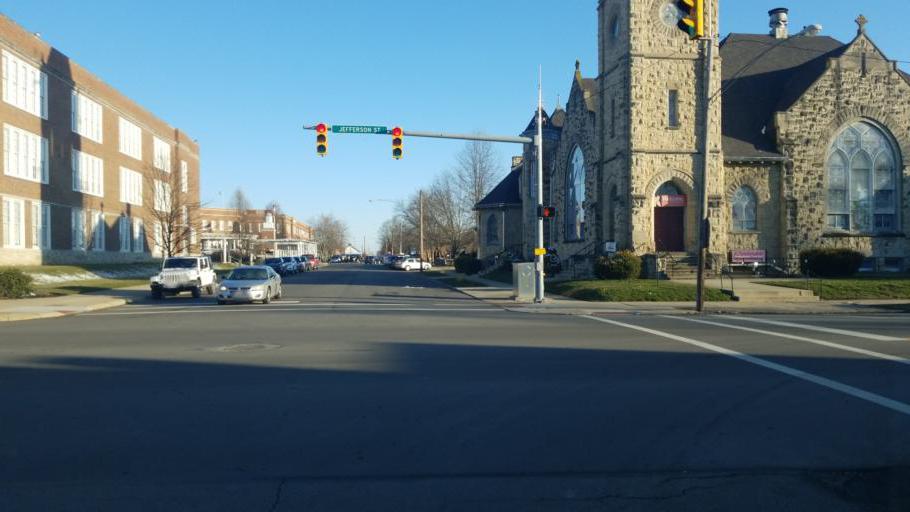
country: US
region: Ohio
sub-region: Highland County
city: Greenfield
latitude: 39.3507
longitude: -83.3868
